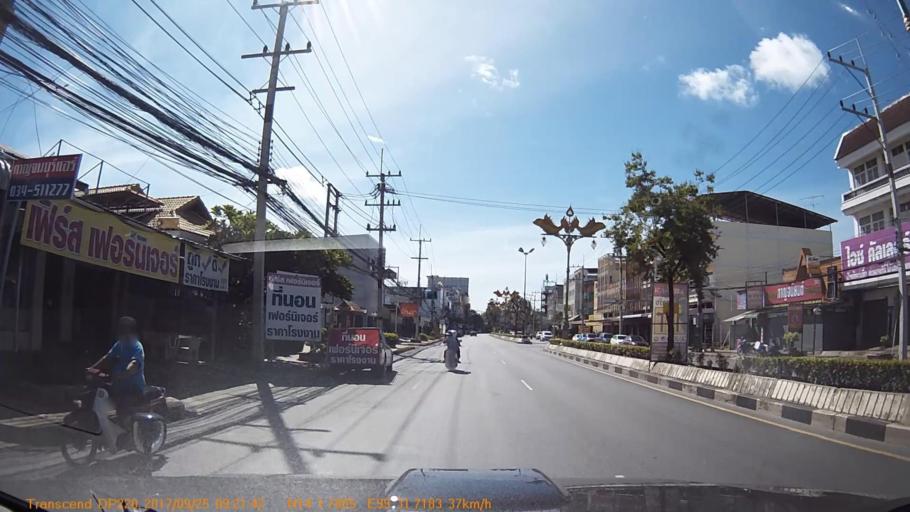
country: TH
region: Kanchanaburi
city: Kanchanaburi
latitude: 14.0296
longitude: 99.5288
